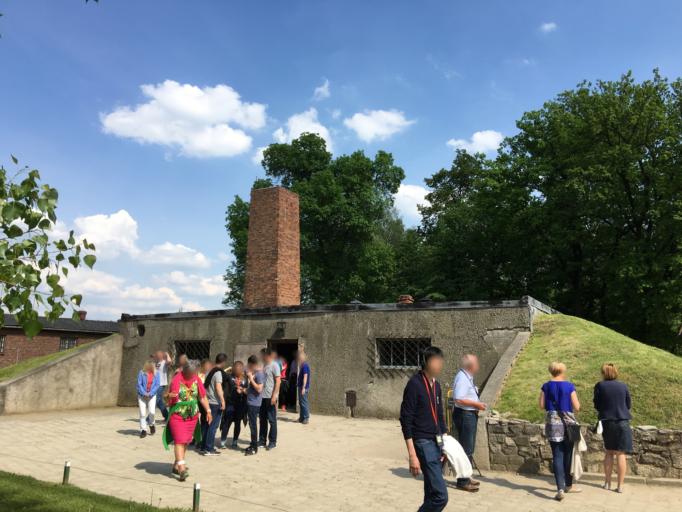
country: PL
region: Lesser Poland Voivodeship
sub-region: Powiat oswiecimski
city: Oswiecim
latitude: 50.0282
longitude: 19.2045
